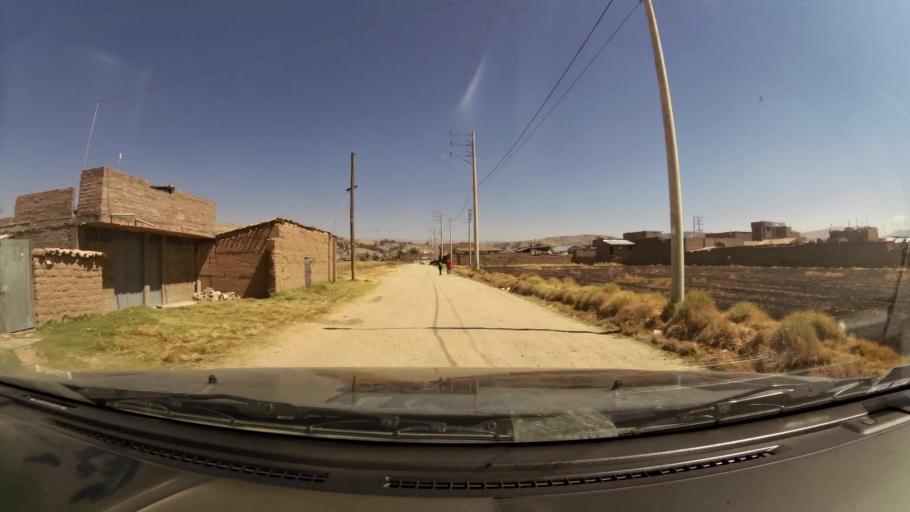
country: PE
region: Junin
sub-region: Provincia de Jauja
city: Jauja
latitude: -11.7793
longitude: -75.4854
